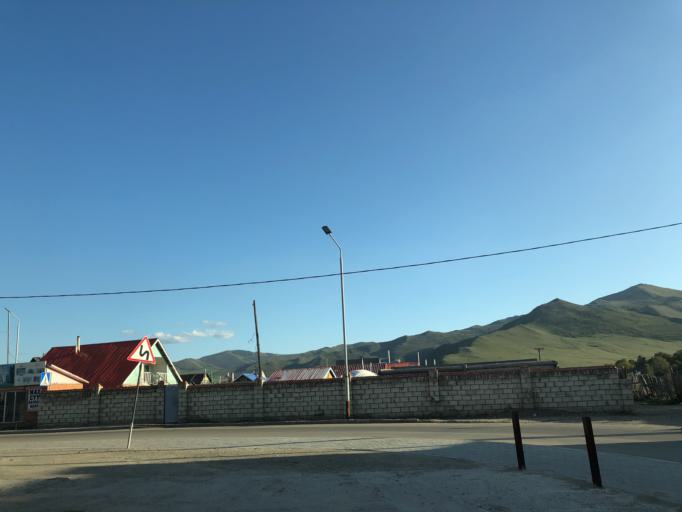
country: MN
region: Ulaanbaatar
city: Ulaanbaatar
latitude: 47.9287
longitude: 107.1616
